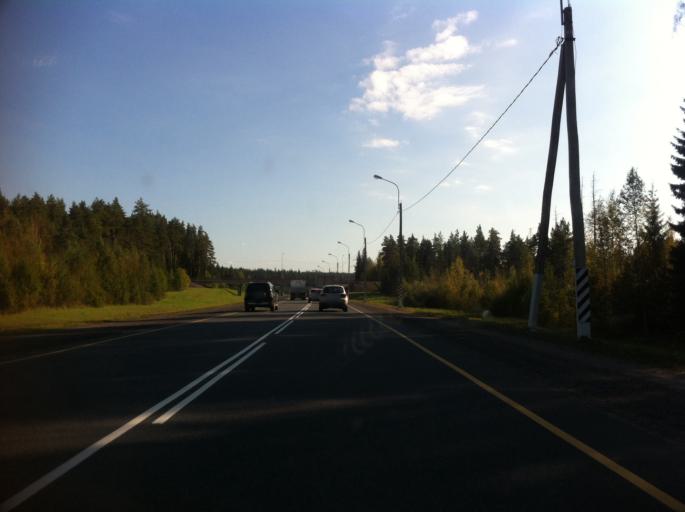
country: RU
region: Leningrad
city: Luga
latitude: 58.7600
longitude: 29.8852
